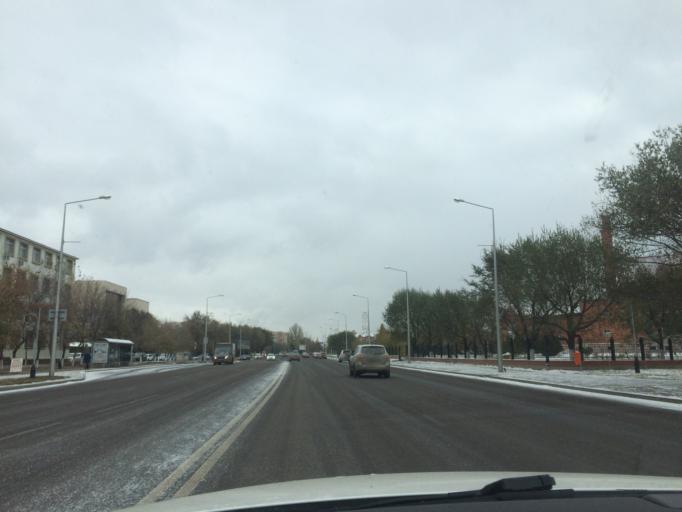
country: KZ
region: Astana Qalasy
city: Astana
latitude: 51.1537
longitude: 71.4501
